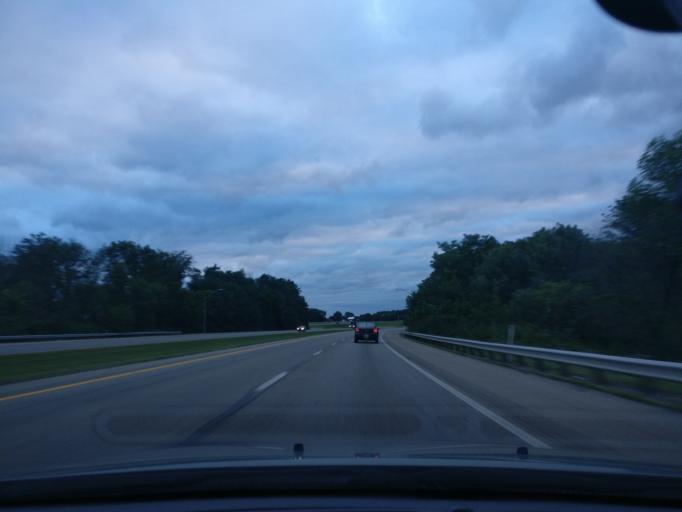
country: US
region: Ohio
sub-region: Greene County
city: Xenia
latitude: 39.6618
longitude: -83.9422
